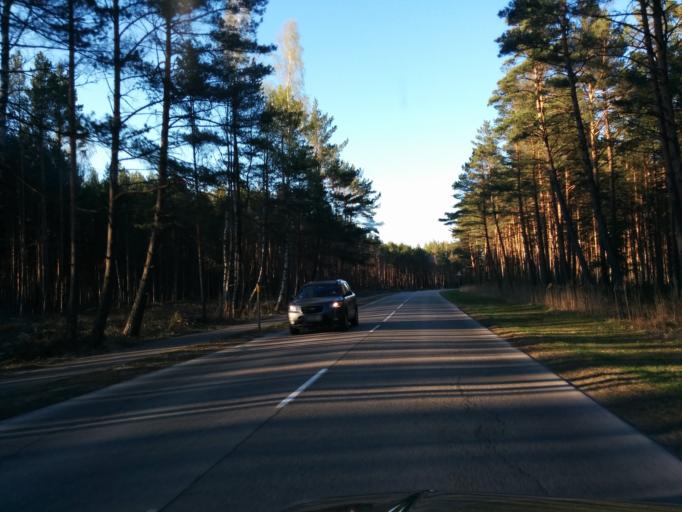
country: LV
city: Tireli
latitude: 56.9690
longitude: 23.5332
